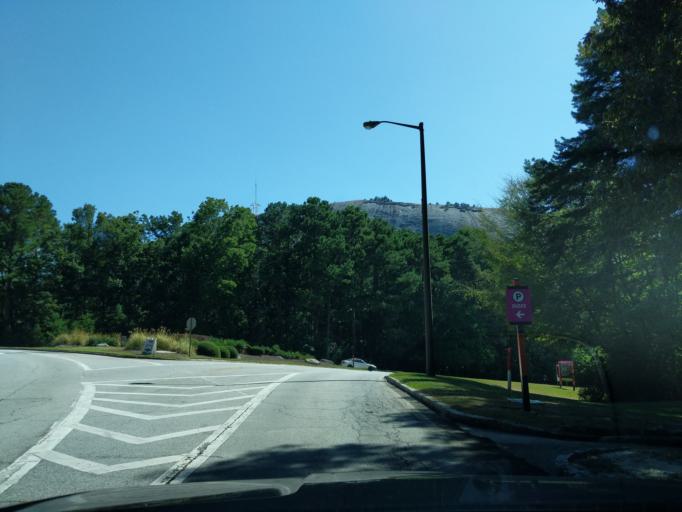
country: US
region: Georgia
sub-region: DeKalb County
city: Stone Mountain
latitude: 33.8148
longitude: -84.1464
